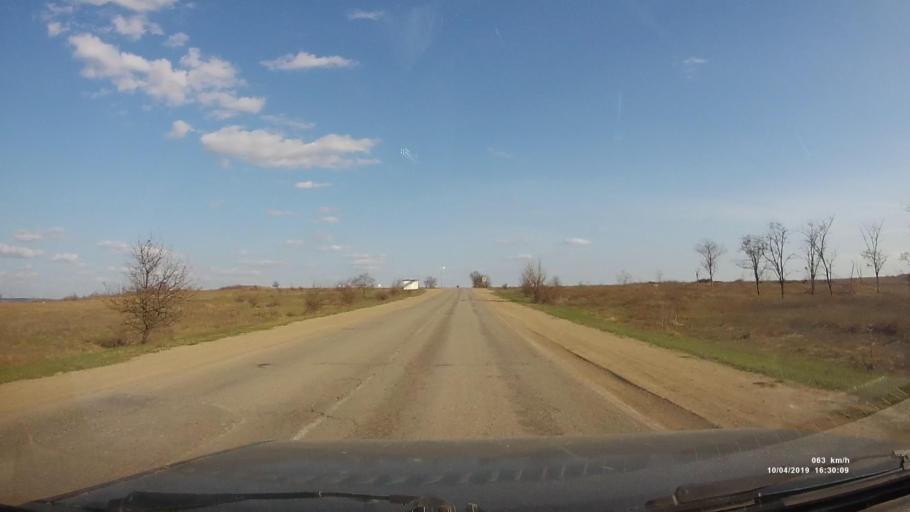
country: RU
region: Rostov
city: Staraya Stanitsa
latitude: 48.2640
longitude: 40.3624
